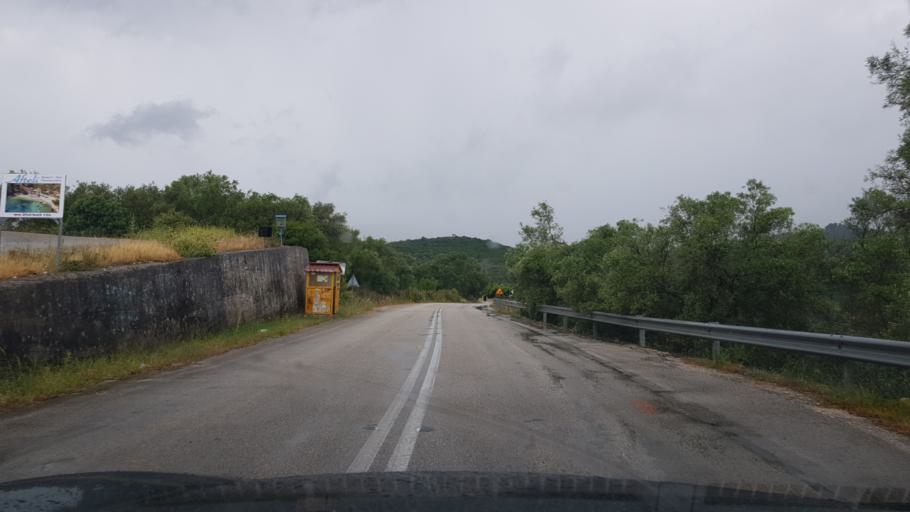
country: GR
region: Ionian Islands
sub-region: Lefkada
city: Nidri
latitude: 38.6338
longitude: 20.6581
